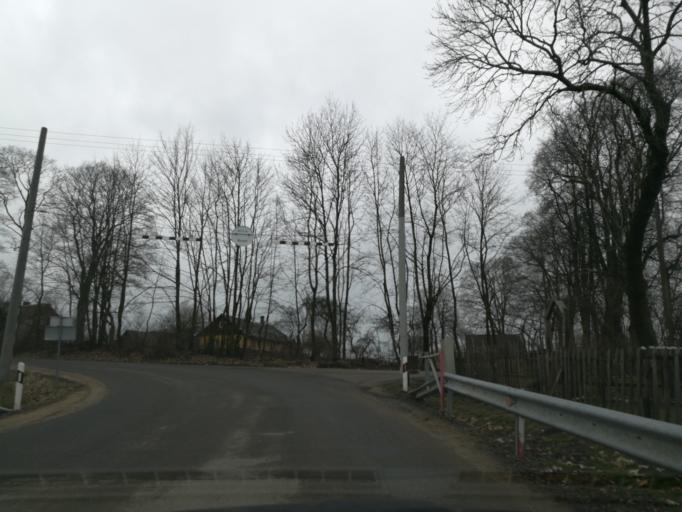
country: LT
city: Lentvaris
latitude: 54.6425
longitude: 25.0257
